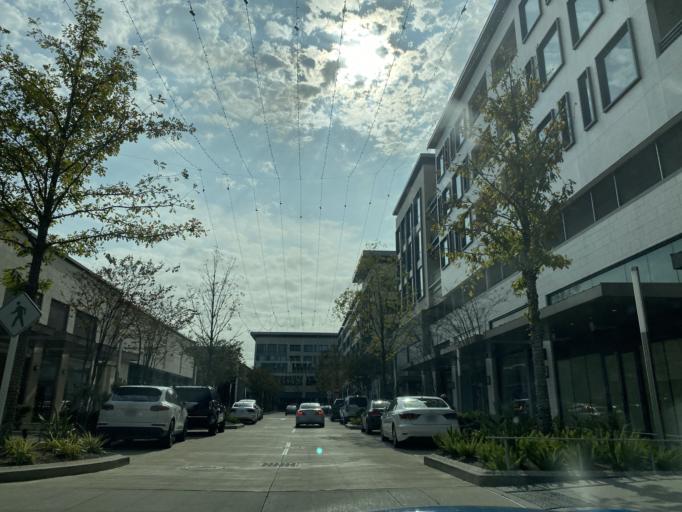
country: US
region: Texas
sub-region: Harris County
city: West University Place
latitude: 29.7434
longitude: -95.4540
